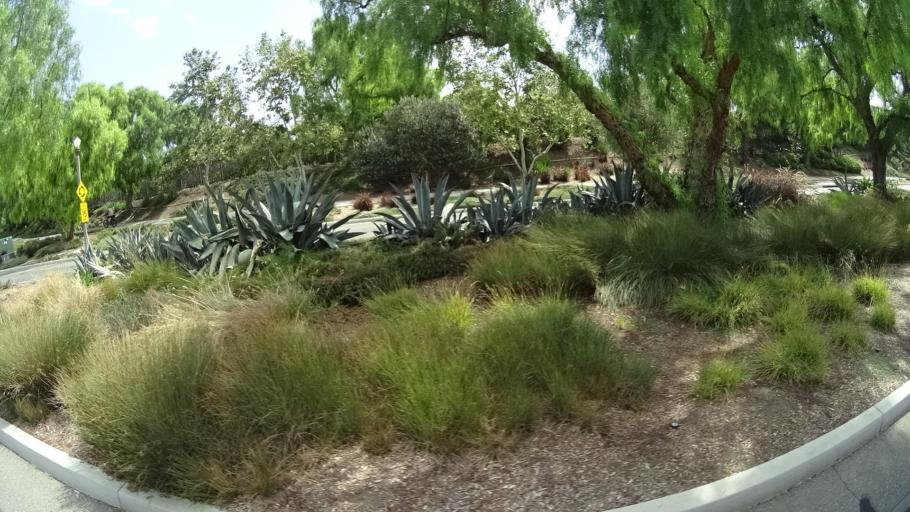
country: US
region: California
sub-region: Orange County
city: San Juan Capistrano
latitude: 33.5209
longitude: -117.6281
